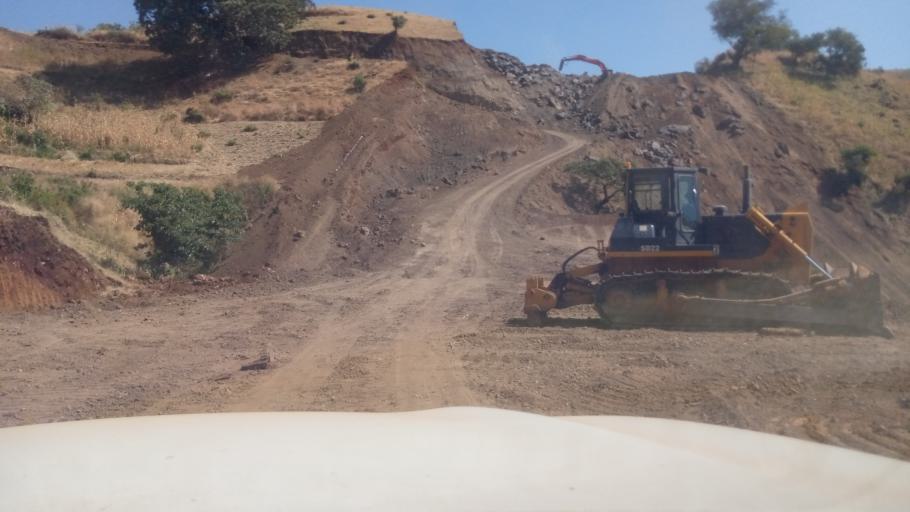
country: ET
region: Amhara
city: Debark'
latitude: 13.3014
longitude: 37.8259
